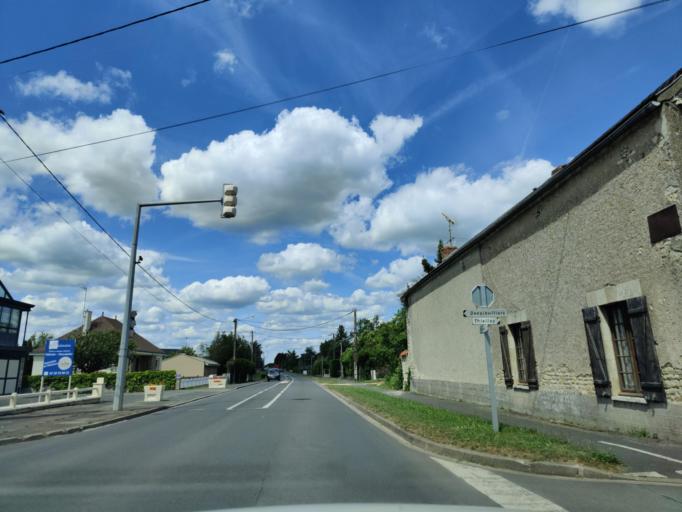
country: FR
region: Centre
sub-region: Departement du Loiret
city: Dadonville
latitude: 48.1404
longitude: 2.2558
